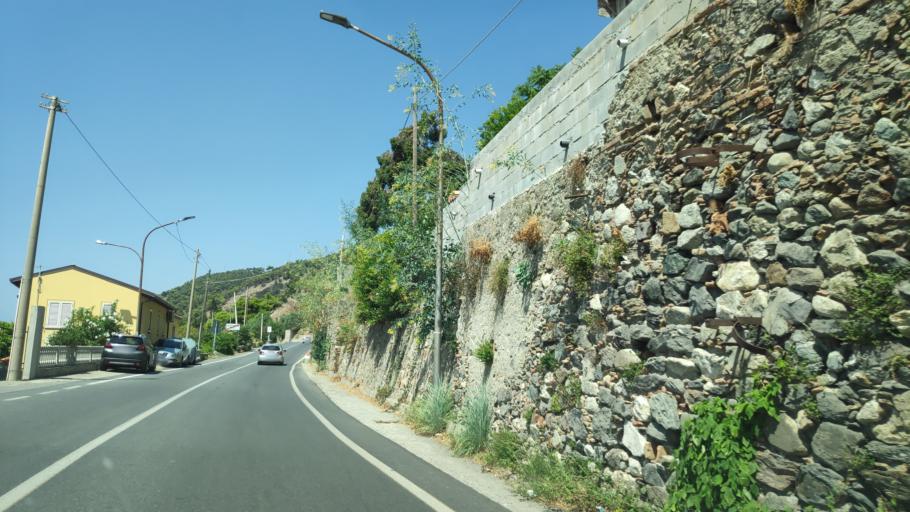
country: IT
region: Calabria
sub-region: Provincia di Reggio Calabria
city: Palizzi Marina
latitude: 37.9195
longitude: 15.9777
